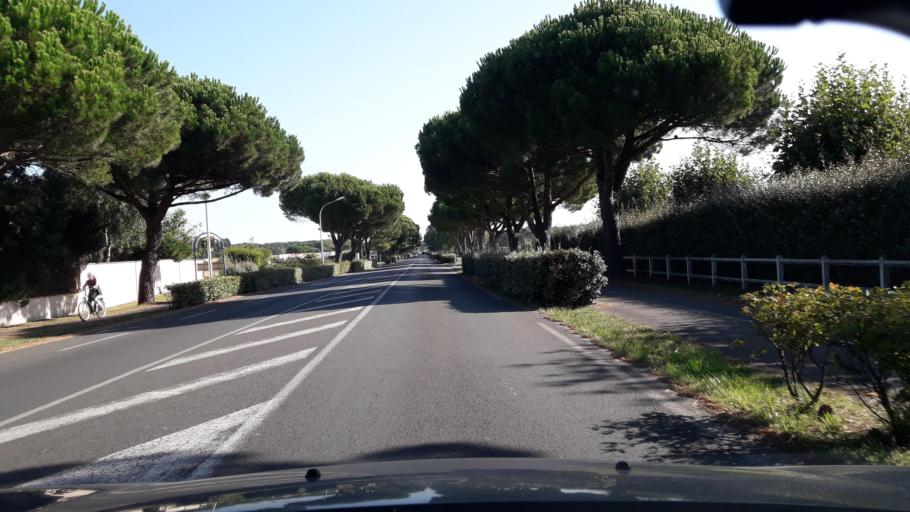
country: FR
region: Poitou-Charentes
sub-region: Departement de la Charente-Maritime
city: Les Mathes
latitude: 45.6953
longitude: -1.1763
